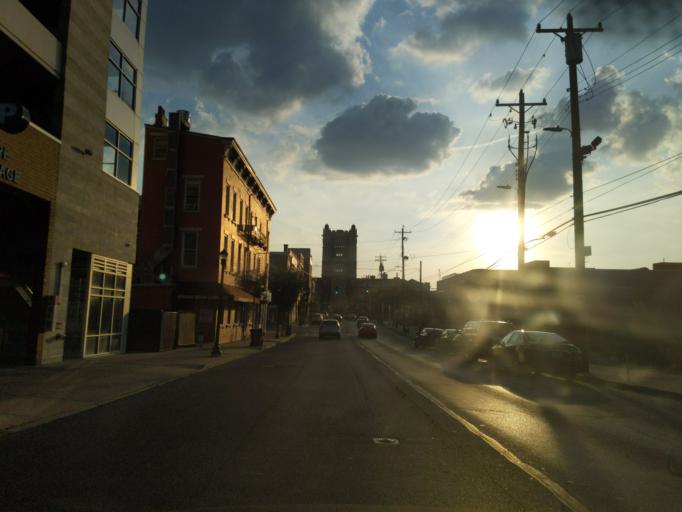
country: US
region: Ohio
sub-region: Hamilton County
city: Saint Bernard
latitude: 39.1285
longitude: -84.5184
